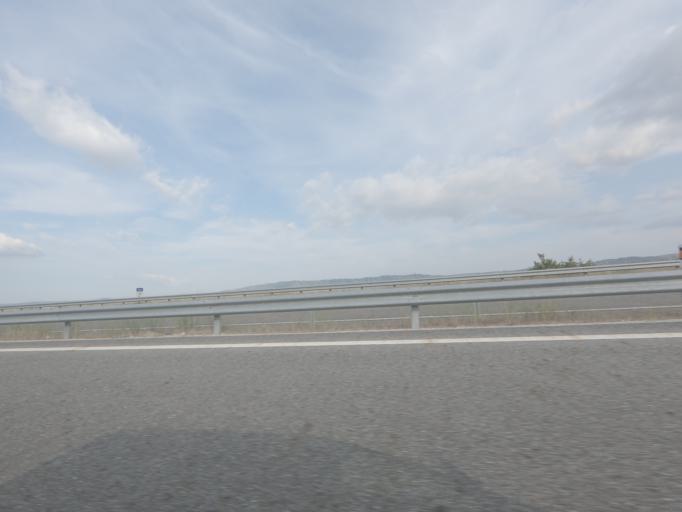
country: PT
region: Vila Real
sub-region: Chaves
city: Chaves
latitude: 41.7288
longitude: -7.5348
